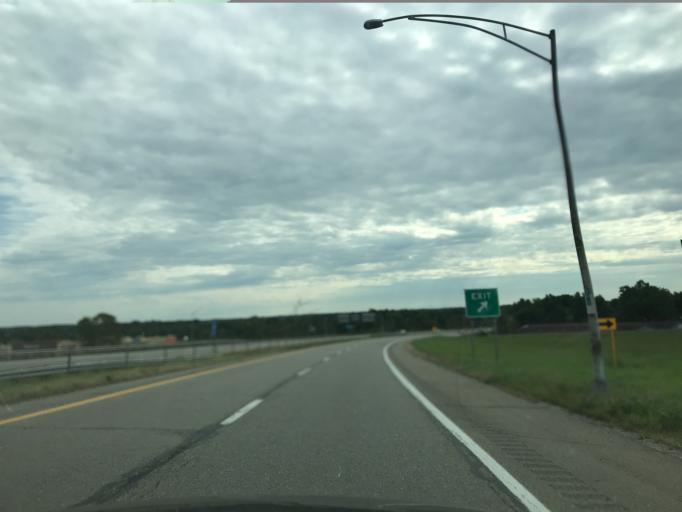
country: US
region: Ohio
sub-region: Trumbull County
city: Morgandale
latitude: 41.2740
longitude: -80.7772
